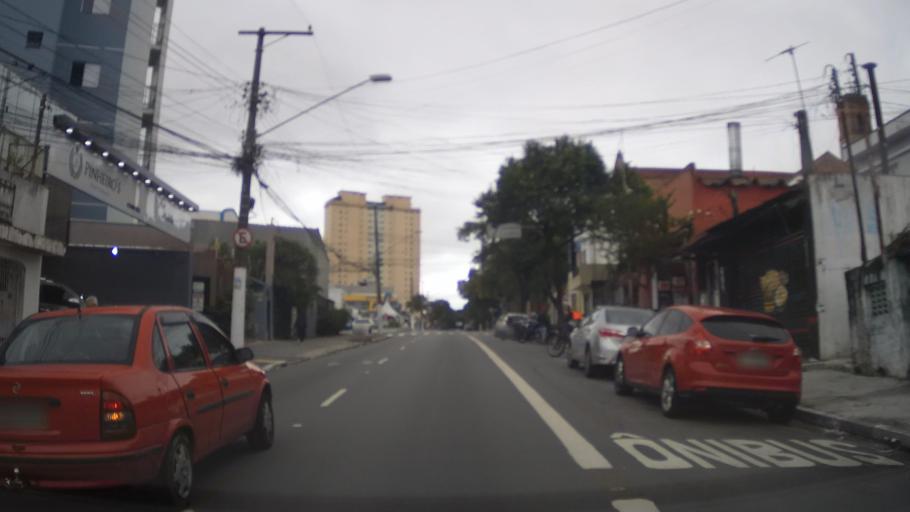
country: BR
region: Sao Paulo
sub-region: Guarulhos
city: Guarulhos
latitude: -23.5286
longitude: -46.5272
